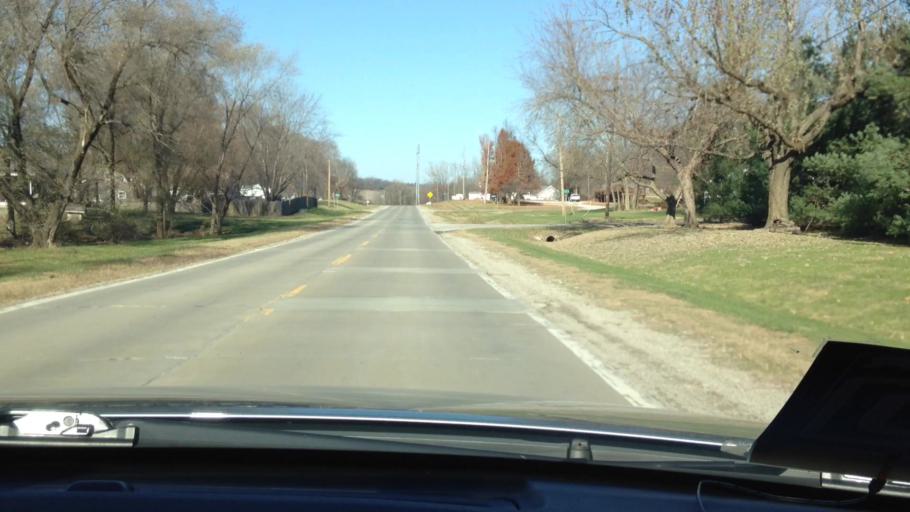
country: US
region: Missouri
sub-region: Platte County
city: Platte City
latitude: 39.4979
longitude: -94.8012
